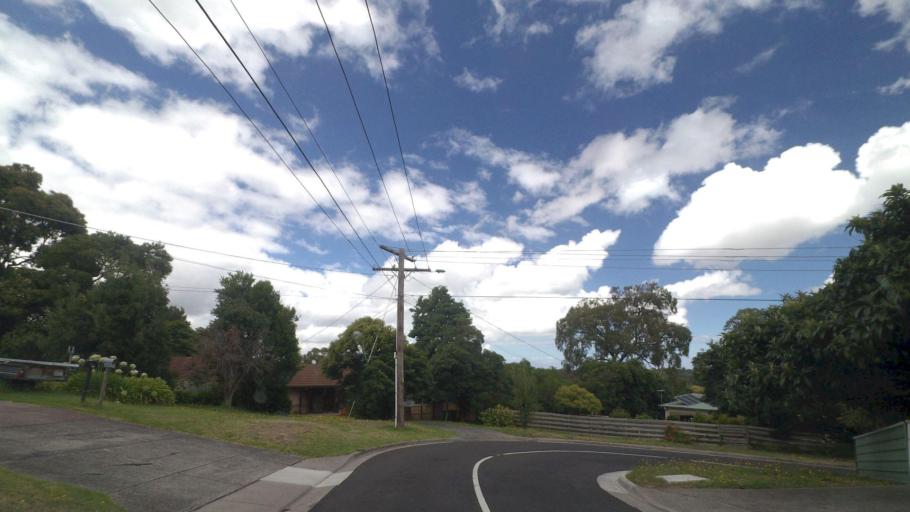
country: AU
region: Victoria
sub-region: Knox
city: Boronia
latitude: -37.8666
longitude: 145.2896
